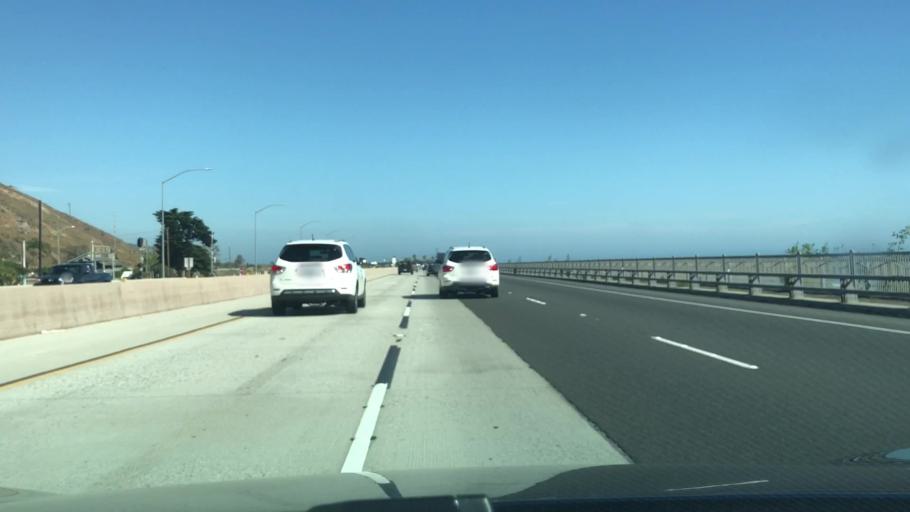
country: US
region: California
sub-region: Santa Barbara County
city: Carpinteria
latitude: 34.3628
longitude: -119.4484
